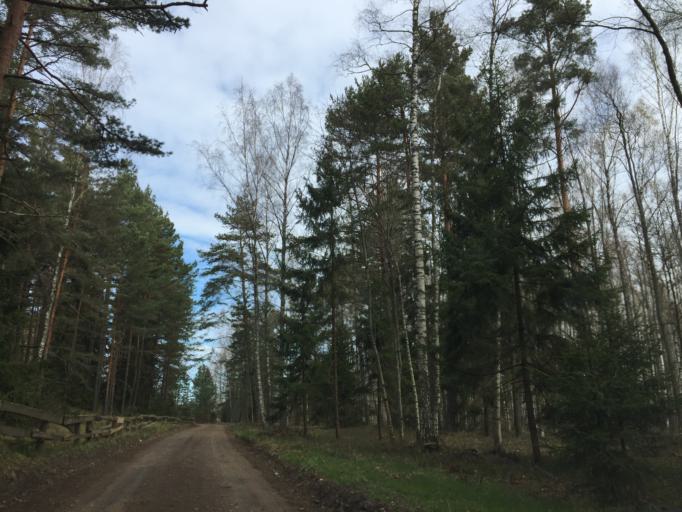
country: LV
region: Salacgrivas
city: Salacgriva
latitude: 57.5399
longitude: 24.3676
